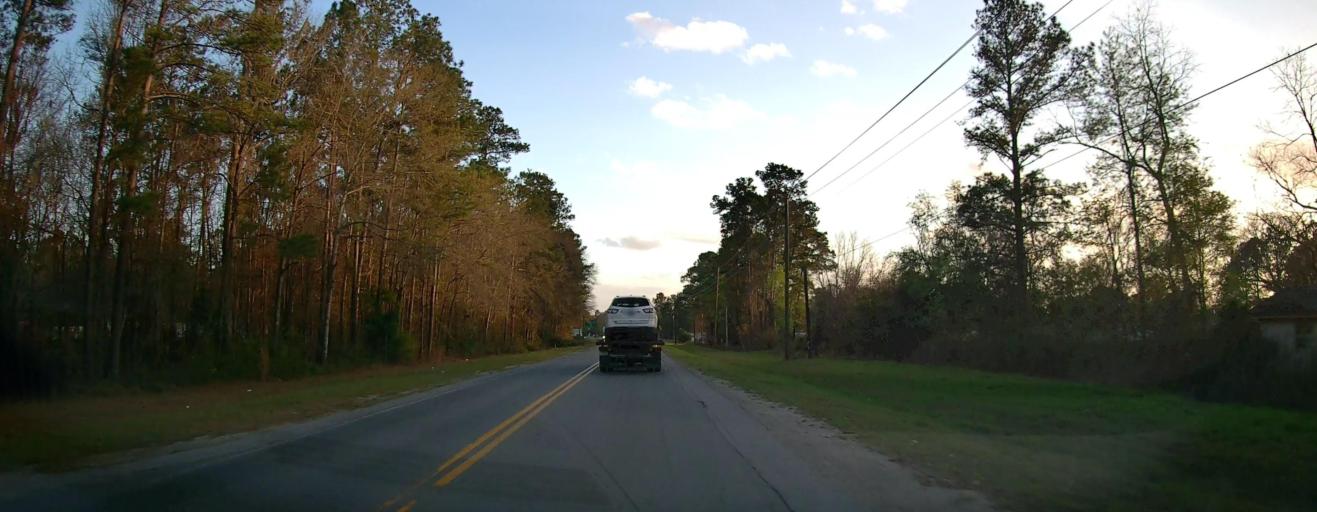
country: US
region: Georgia
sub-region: Chatham County
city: Bloomingdale
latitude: 32.1474
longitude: -81.3898
